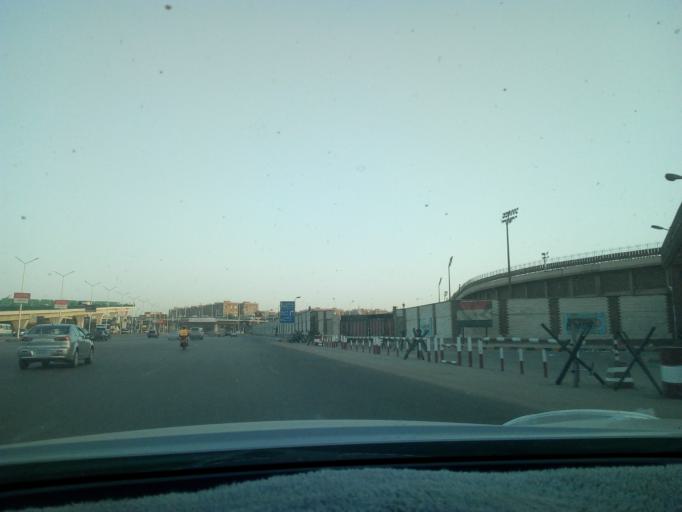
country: EG
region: Muhafazat al Qalyubiyah
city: Al Khankah
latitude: 30.1129
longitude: 31.3678
